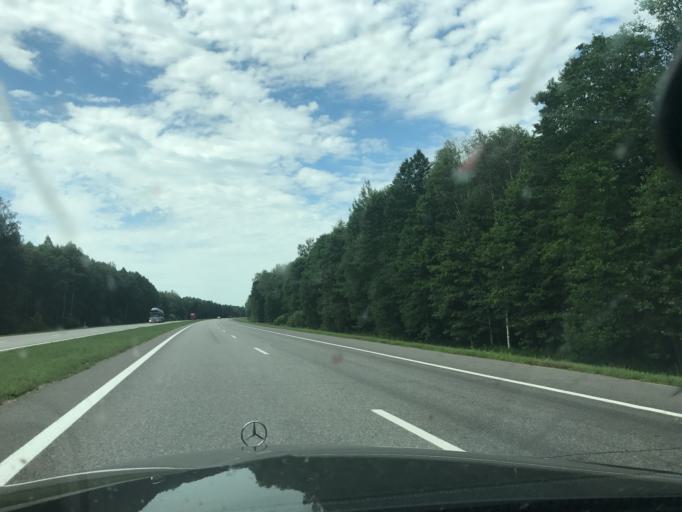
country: BY
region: Minsk
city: Horad Zhodzina
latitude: 54.0521
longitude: 28.4312
